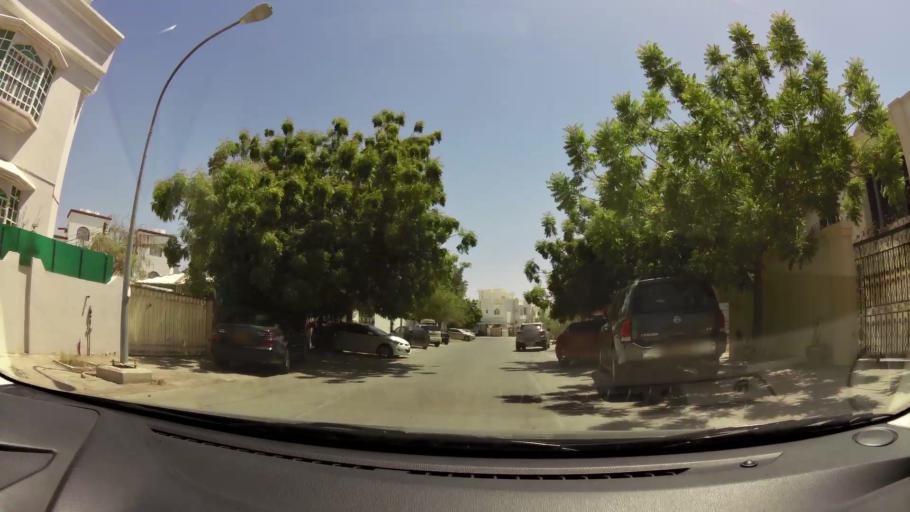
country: OM
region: Muhafazat Masqat
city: Bawshar
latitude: 23.5997
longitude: 58.3745
